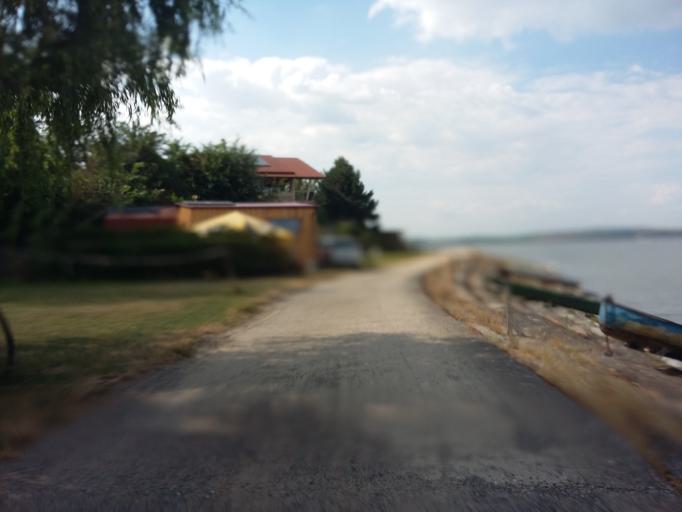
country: CZ
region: South Moravian
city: Sakvice
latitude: 48.8818
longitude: 16.6731
